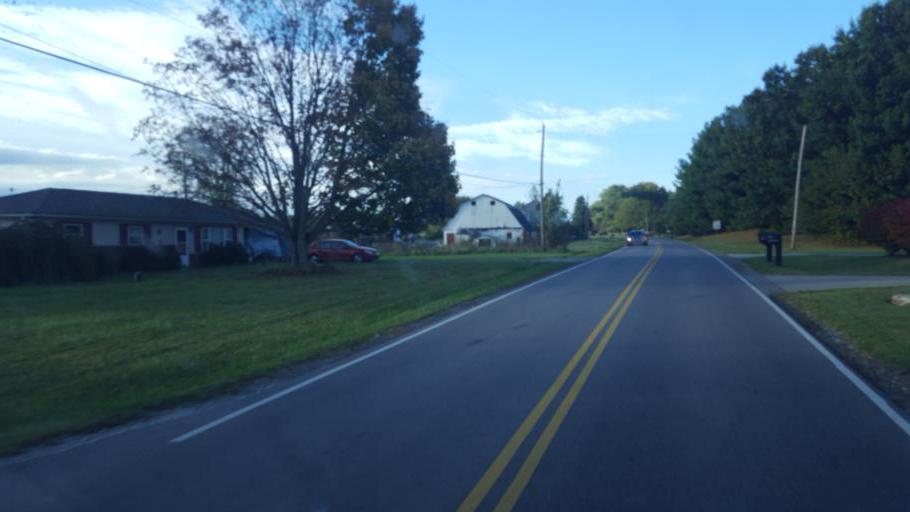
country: US
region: Ohio
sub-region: Licking County
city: Pataskala
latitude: 40.0337
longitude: -82.7315
